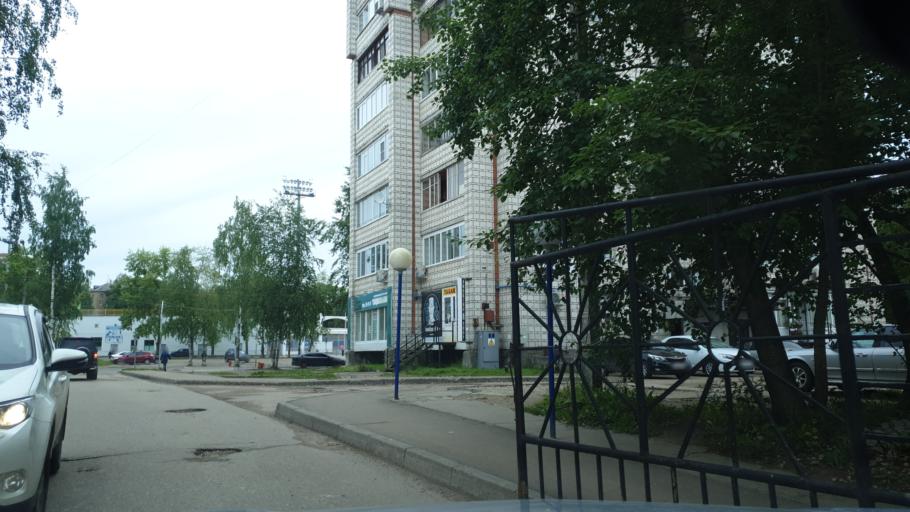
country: RU
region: Komi Republic
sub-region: Syktyvdinskiy Rayon
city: Syktyvkar
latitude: 61.6626
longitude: 50.8300
